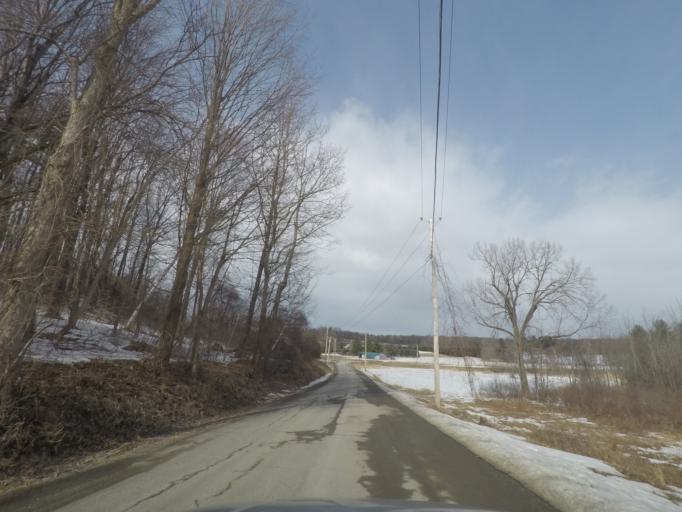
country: US
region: New York
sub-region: Saratoga County
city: Waterford
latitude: 42.7881
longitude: -73.5852
